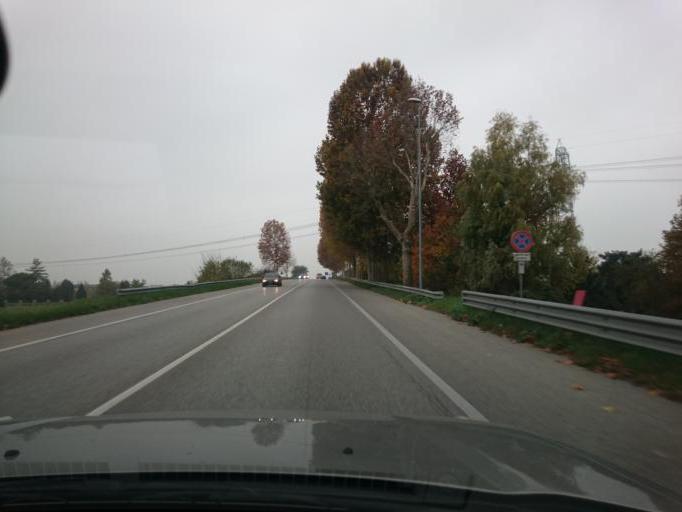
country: IT
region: Veneto
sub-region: Provincia di Padova
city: Legnaro
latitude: 45.3575
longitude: 11.9460
